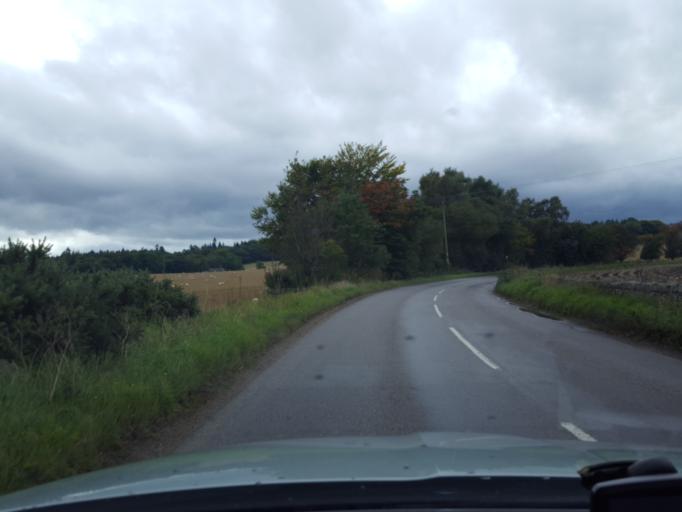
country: GB
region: Scotland
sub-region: Aberdeenshire
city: Kemnay
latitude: 57.1700
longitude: -2.4162
